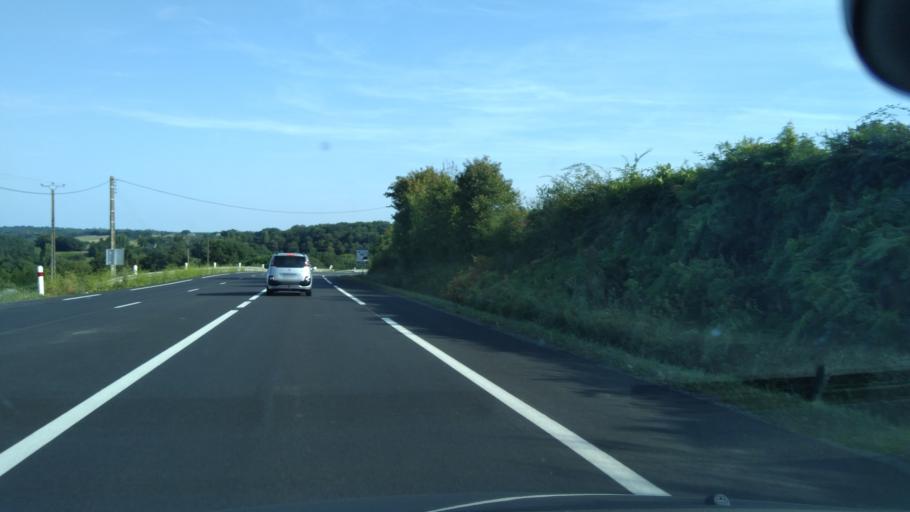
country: FR
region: Pays de la Loire
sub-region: Departement de la Mayenne
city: Entrammes
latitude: 47.9751
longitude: -0.7073
